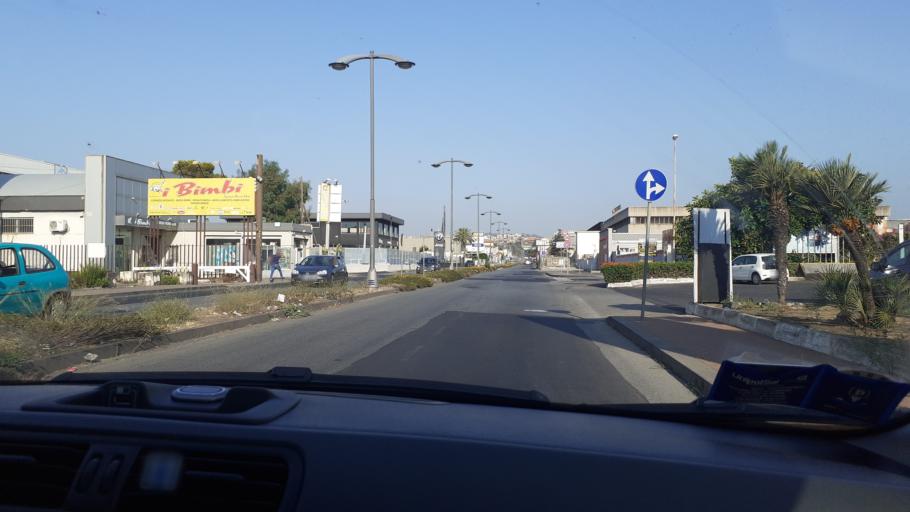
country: IT
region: Sicily
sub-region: Catania
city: Misterbianco
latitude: 37.5123
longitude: 15.0310
